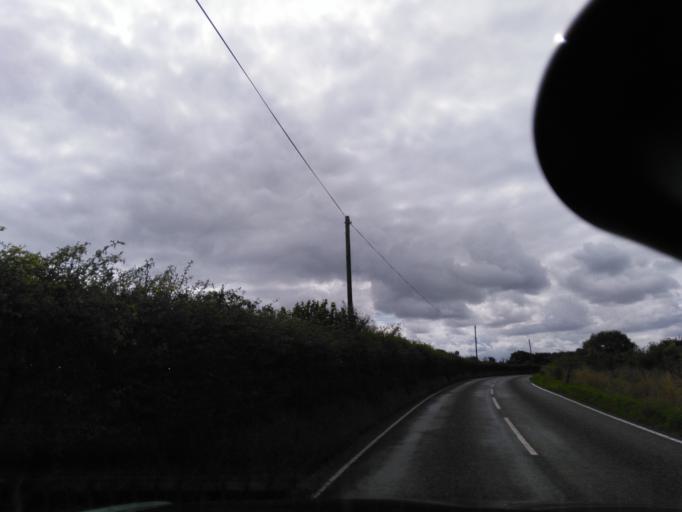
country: GB
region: England
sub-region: Dorset
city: Blandford Forum
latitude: 50.9010
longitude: -2.1552
